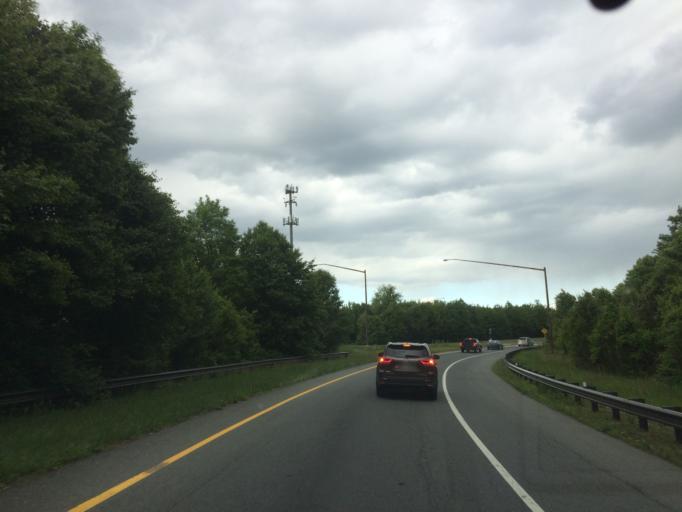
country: US
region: Maryland
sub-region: Montgomery County
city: Germantown
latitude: 39.1986
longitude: -77.2598
